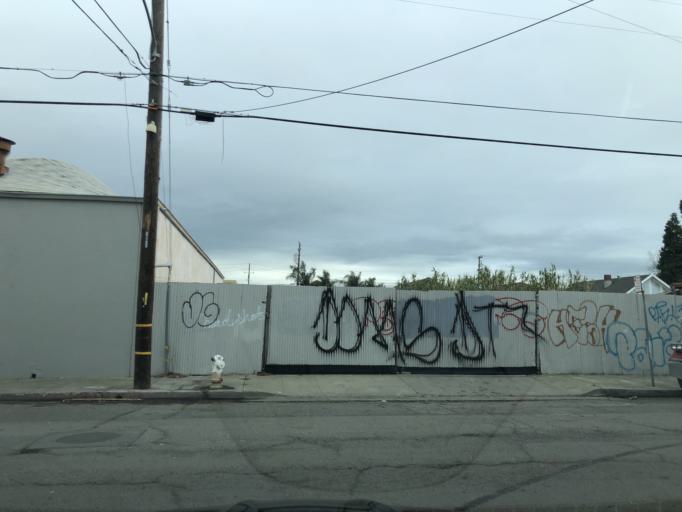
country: US
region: California
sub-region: Alameda County
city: San Leandro
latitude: 37.7367
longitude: -122.1795
